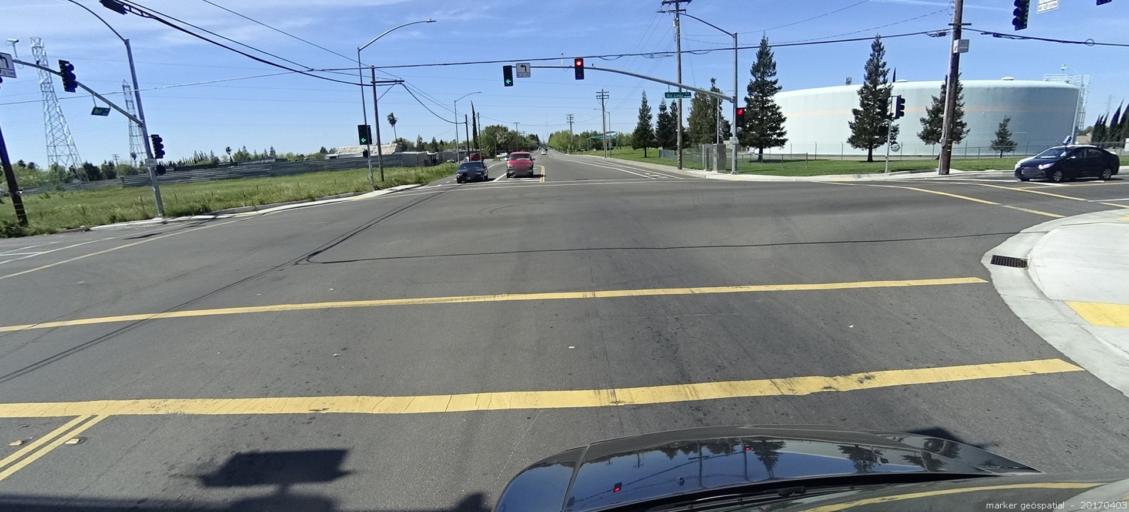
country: US
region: California
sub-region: Sacramento County
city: Rio Linda
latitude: 38.6476
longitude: -121.4476
